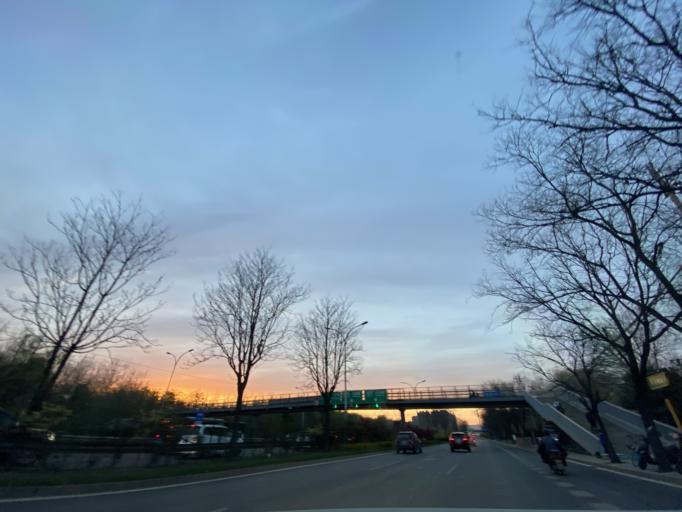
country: CN
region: Beijing
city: Qinghe
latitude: 40.0162
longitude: 116.3522
